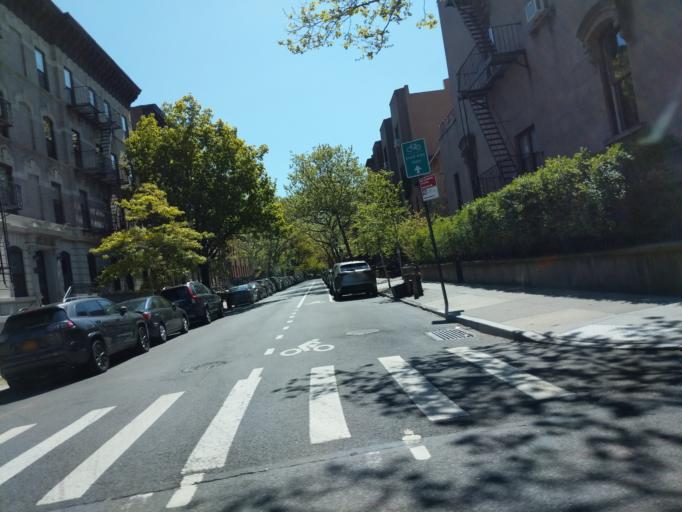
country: US
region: New York
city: New York City
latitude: 40.6829
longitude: -73.9978
